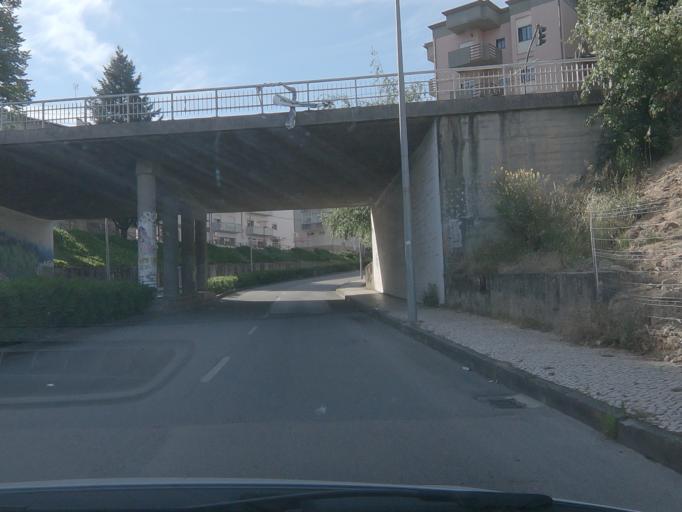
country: PT
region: Viseu
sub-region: Viseu
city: Viseu
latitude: 40.6500
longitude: -7.9098
